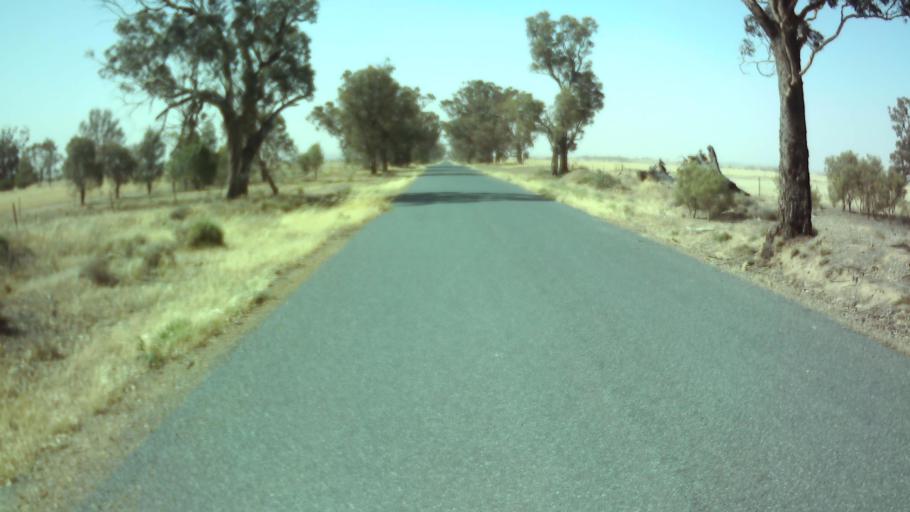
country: AU
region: New South Wales
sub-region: Weddin
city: Grenfell
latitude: -33.8937
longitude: 147.9220
